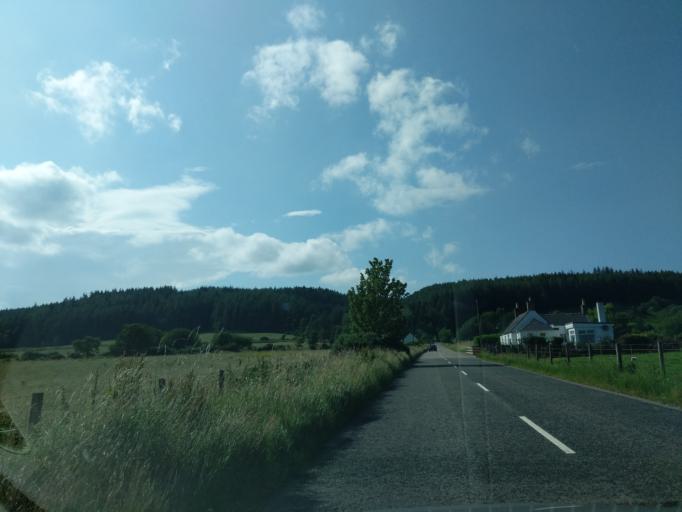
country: GB
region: Scotland
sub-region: Moray
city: Rothes
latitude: 57.5524
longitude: -3.1476
